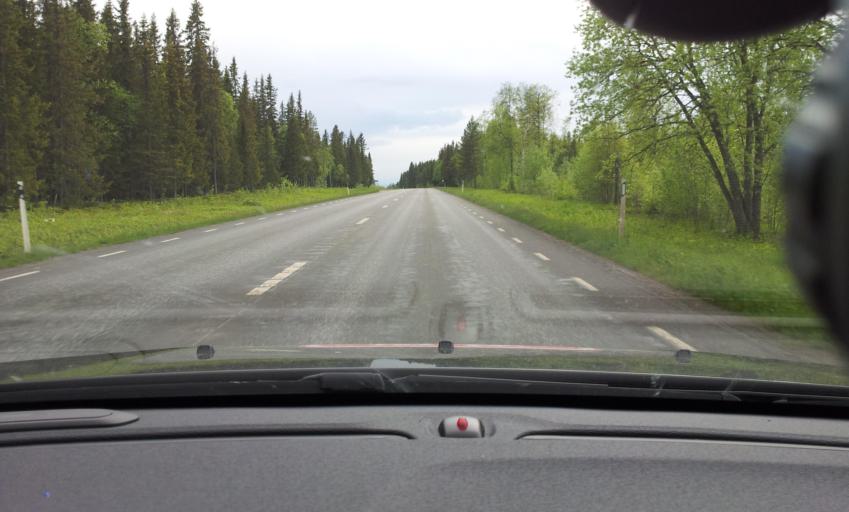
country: SE
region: Jaemtland
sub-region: OEstersunds Kommun
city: Lit
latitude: 63.1952
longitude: 14.7684
